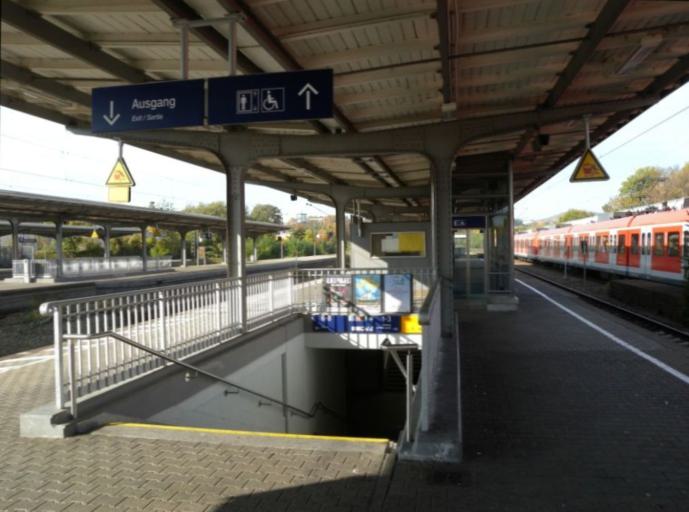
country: DE
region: Baden-Wuerttemberg
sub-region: Regierungsbezirk Stuttgart
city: Stuttgart-Ost
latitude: 48.8012
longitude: 9.2178
